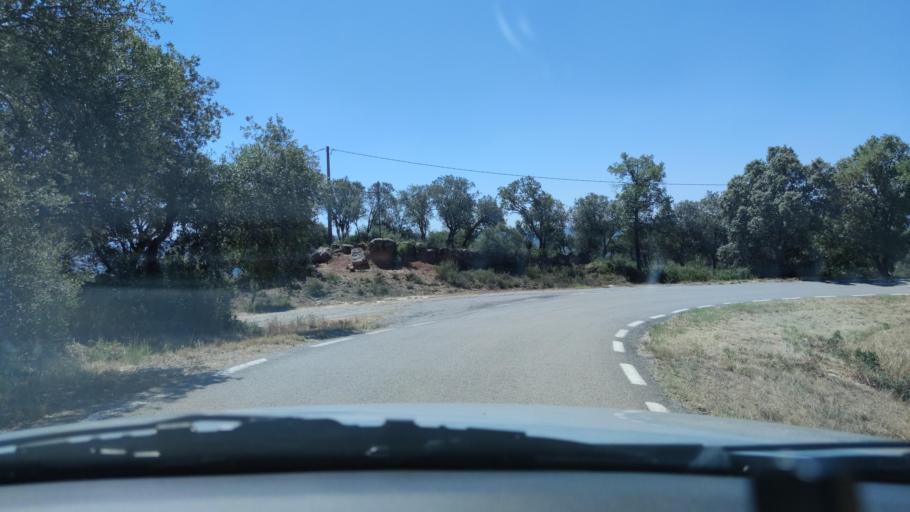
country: ES
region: Catalonia
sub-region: Provincia de Lleida
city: Tora de Riubregos
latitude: 41.8636
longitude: 1.4349
